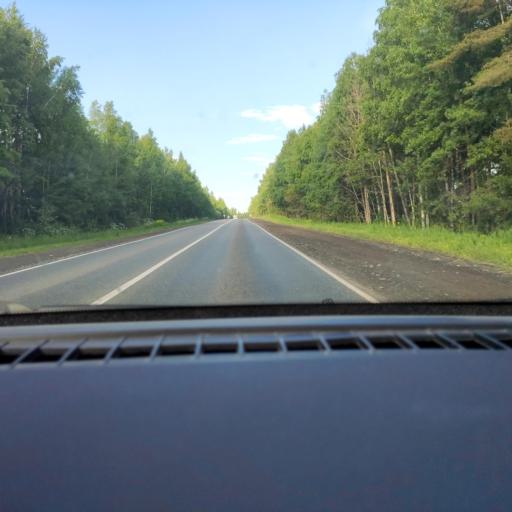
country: RU
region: Udmurtiya
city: Votkinsk
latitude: 56.9799
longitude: 53.7667
